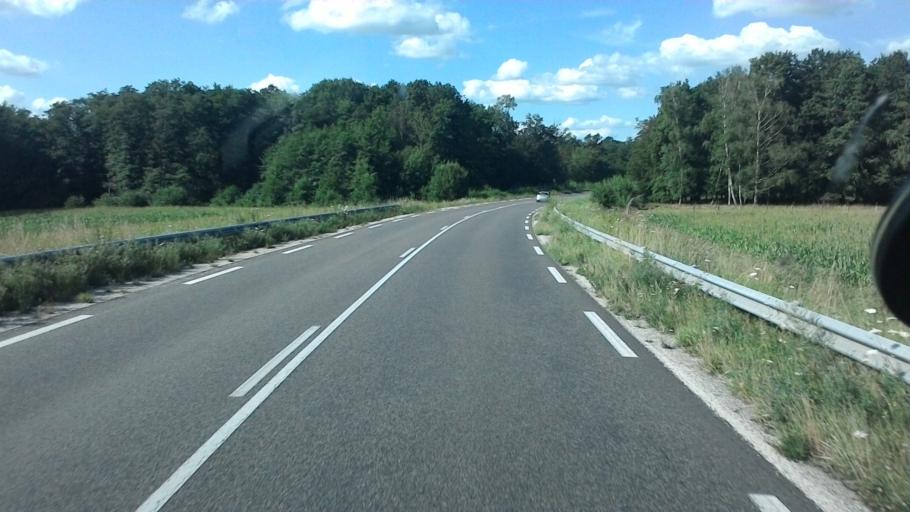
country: FR
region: Franche-Comte
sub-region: Departement de la Haute-Saone
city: Rioz
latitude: 47.4933
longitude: 5.9356
